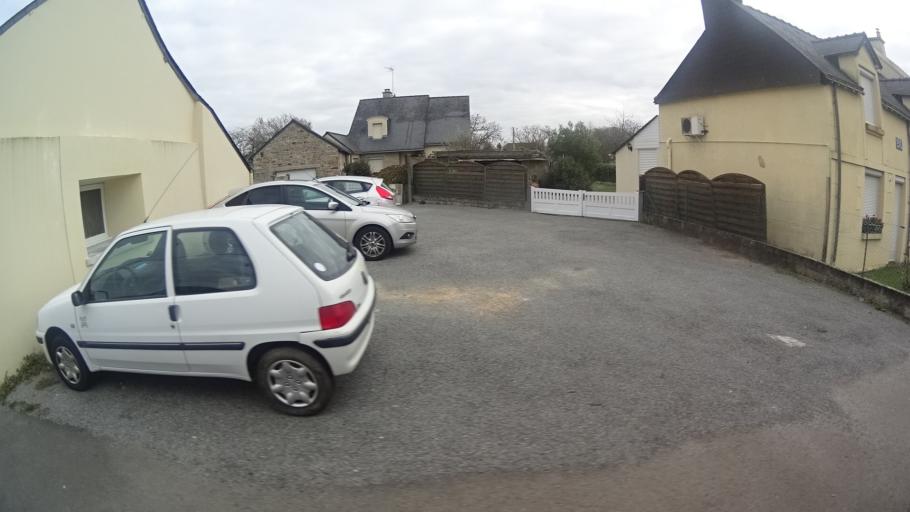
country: FR
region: Brittany
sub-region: Departement d'Ille-et-Vilaine
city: Redon
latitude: 47.6569
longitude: -2.0716
